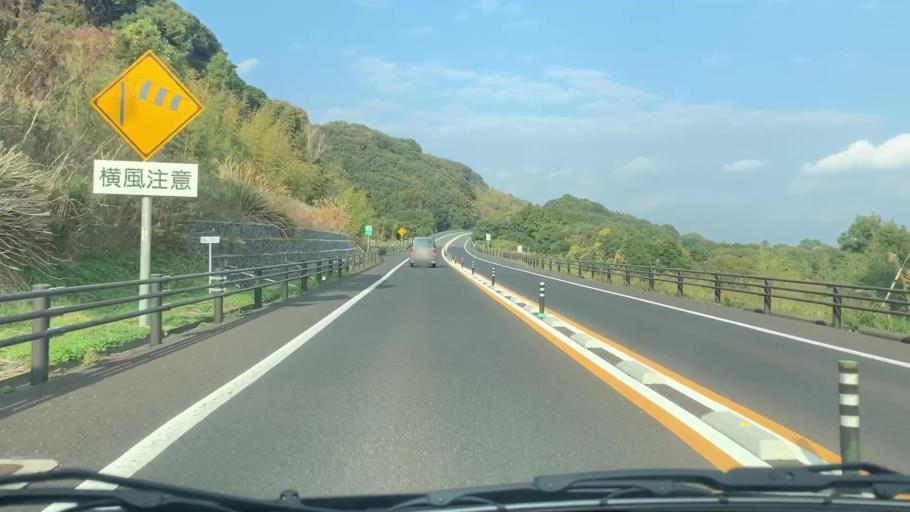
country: JP
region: Nagasaki
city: Sasebo
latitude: 33.0289
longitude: 129.7382
